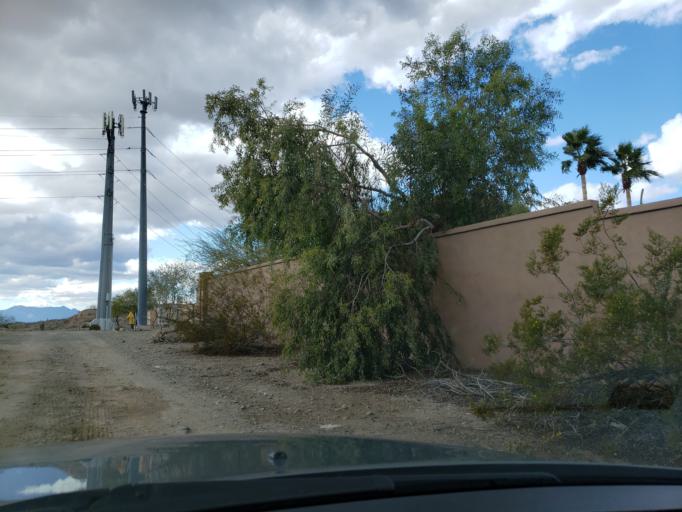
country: US
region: Arizona
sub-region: Maricopa County
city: Laveen
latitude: 33.2927
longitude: -112.0650
